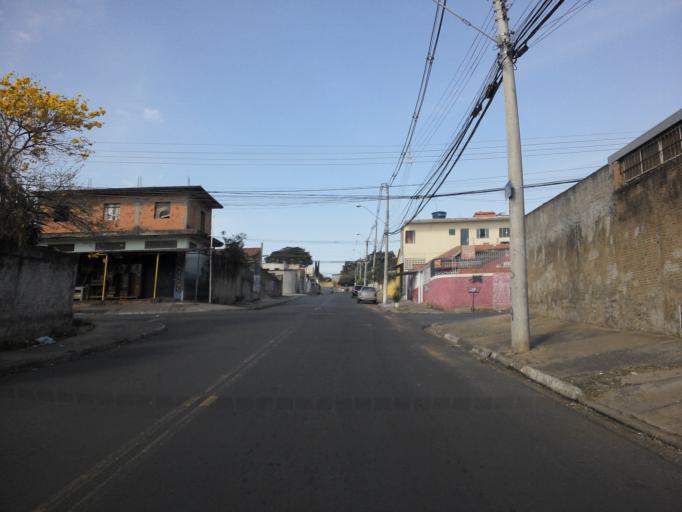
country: BR
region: Sao Paulo
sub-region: Hortolandia
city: Hortolandia
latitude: -22.9023
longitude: -47.2319
